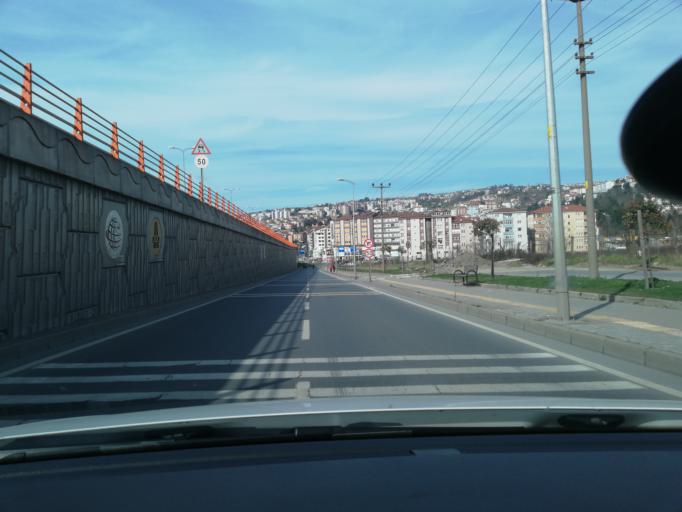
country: TR
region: Zonguldak
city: Eregli
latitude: 41.2671
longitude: 31.4354
